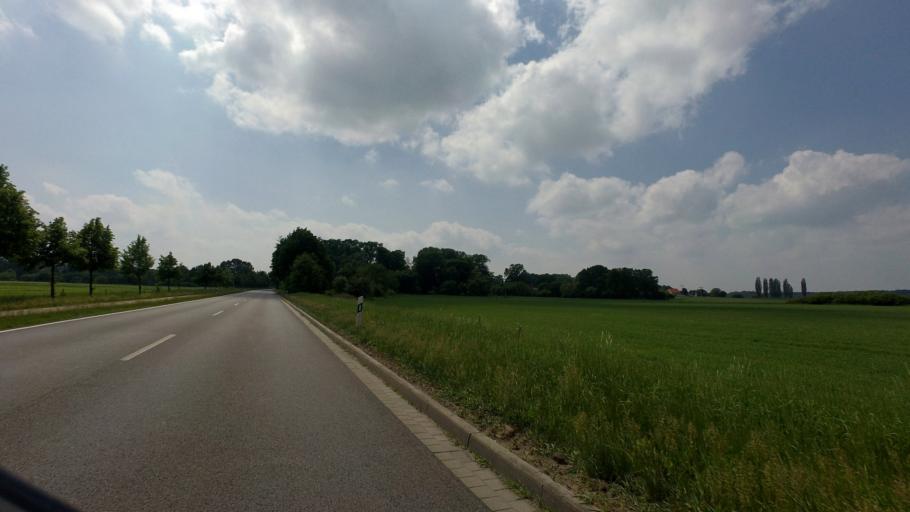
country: DE
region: Brandenburg
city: Cottbus
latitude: 51.6826
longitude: 14.3585
